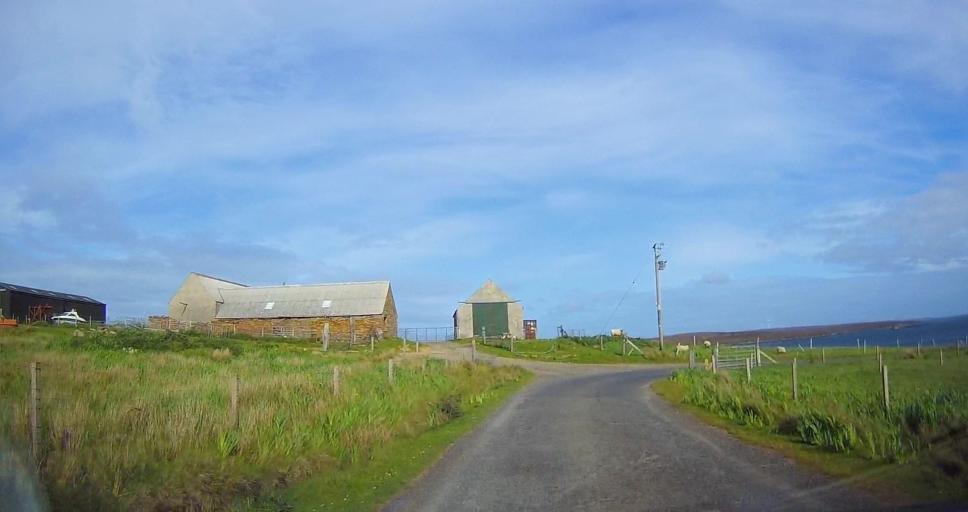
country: GB
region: Scotland
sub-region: Orkney Islands
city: Stromness
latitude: 58.8528
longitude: -3.2042
